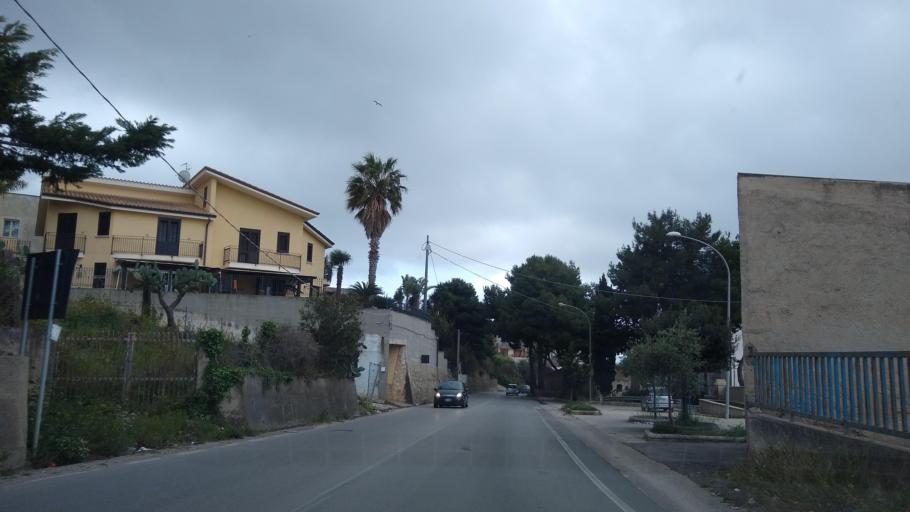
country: IT
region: Sicily
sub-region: Trapani
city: Alcamo
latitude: 37.9791
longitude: 12.9469
